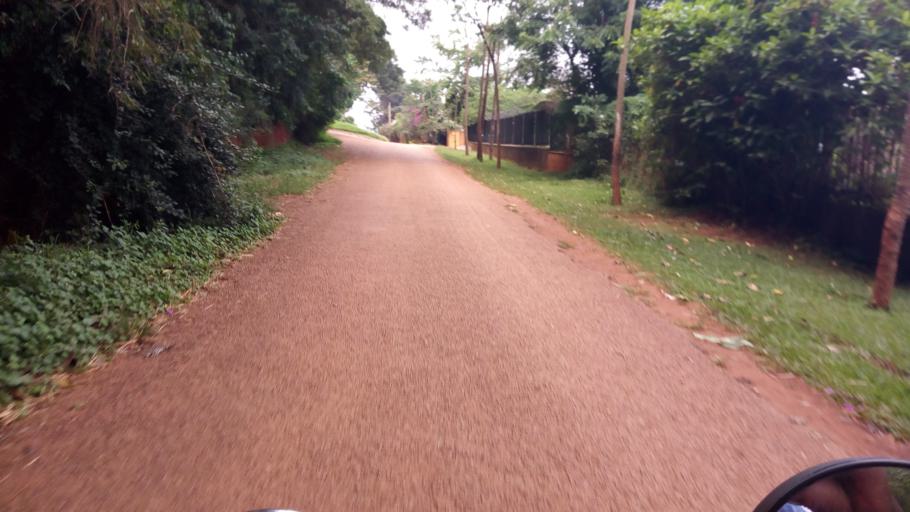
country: UG
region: Central Region
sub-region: Wakiso District
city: Kireka
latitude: 0.3250
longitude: 32.6306
